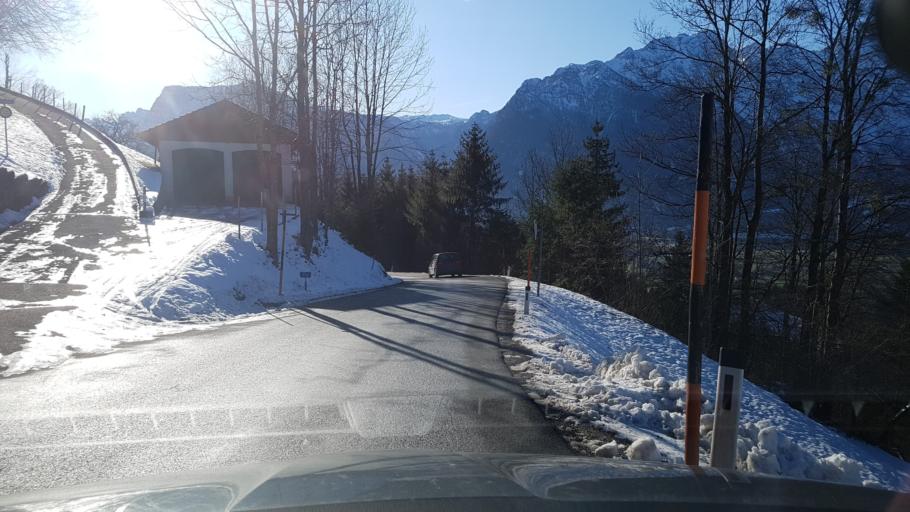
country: AT
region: Salzburg
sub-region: Politischer Bezirk Hallein
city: Golling an der Salzach
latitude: 47.6246
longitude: 13.1908
